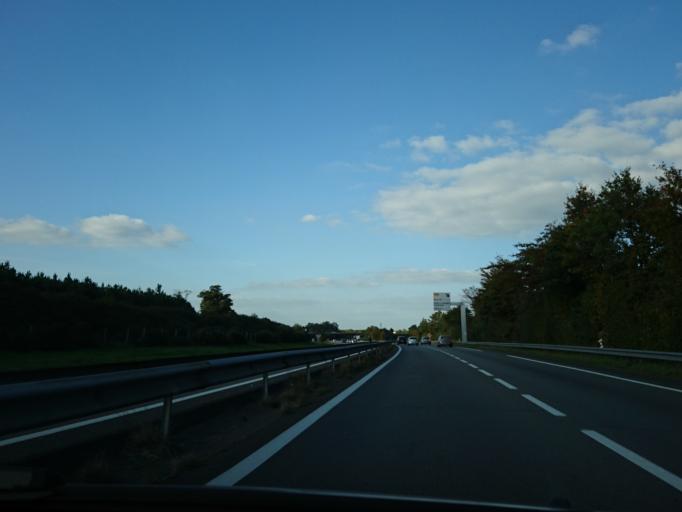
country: FR
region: Pays de la Loire
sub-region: Departement de la Loire-Atlantique
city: Heric
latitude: 47.4114
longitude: -1.6420
